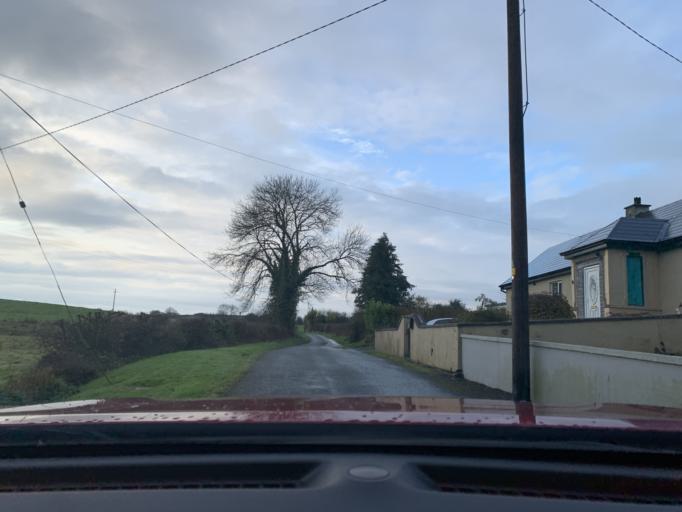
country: IE
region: Connaught
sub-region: Sligo
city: Ballymote
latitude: 54.0470
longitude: -8.5451
